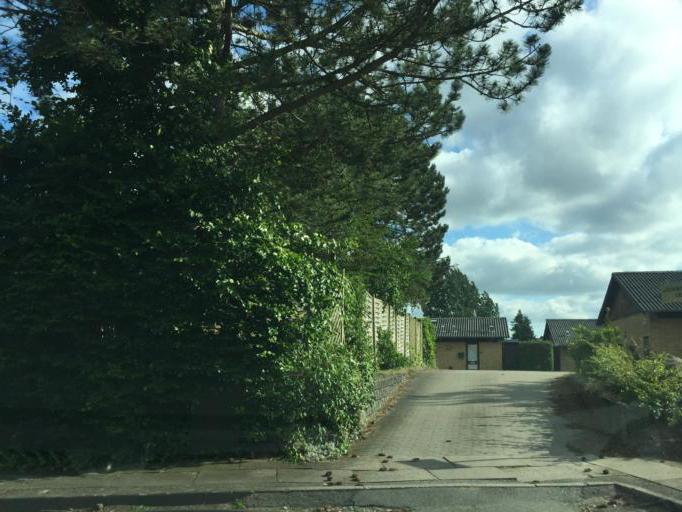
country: DK
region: South Denmark
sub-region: Odense Kommune
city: Odense
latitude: 55.4214
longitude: 10.3625
